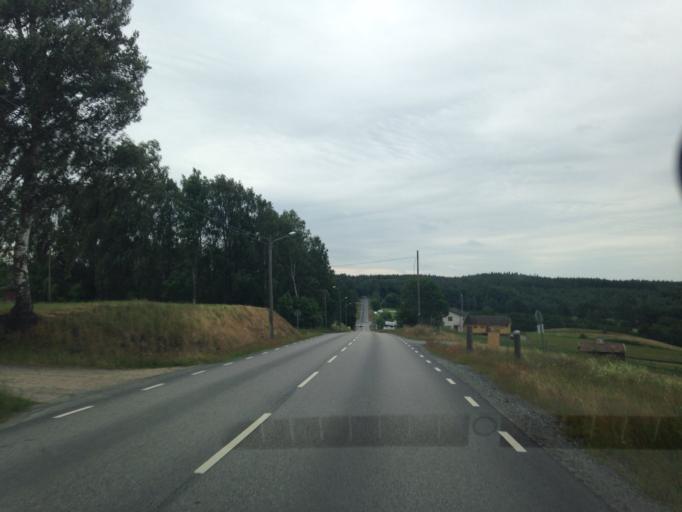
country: SE
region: Vaestra Goetaland
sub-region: Marks Kommun
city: Bua
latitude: 57.5067
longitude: 12.5477
